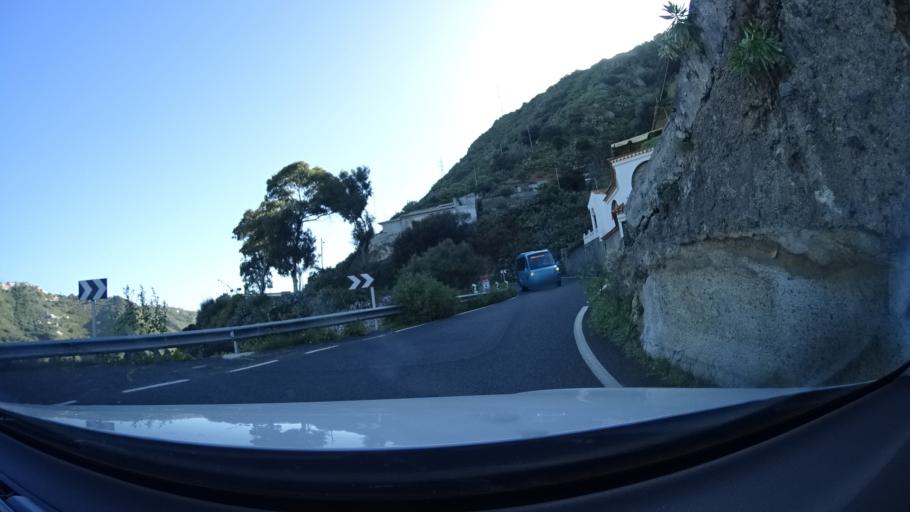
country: ES
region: Canary Islands
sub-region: Provincia de Las Palmas
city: Santa Brigida
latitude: 28.0194
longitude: -15.4717
